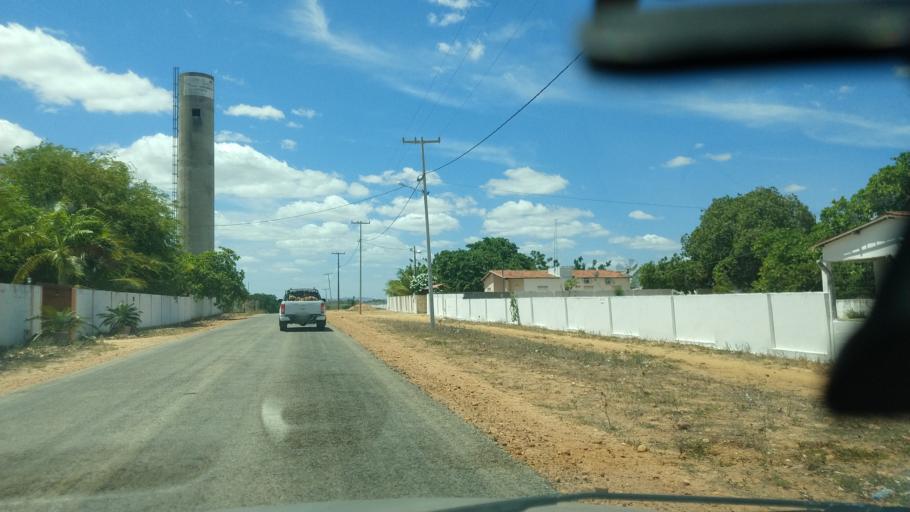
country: BR
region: Rio Grande do Norte
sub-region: Sao Paulo Do Potengi
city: Sao Paulo do Potengi
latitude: -5.9157
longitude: -35.7288
